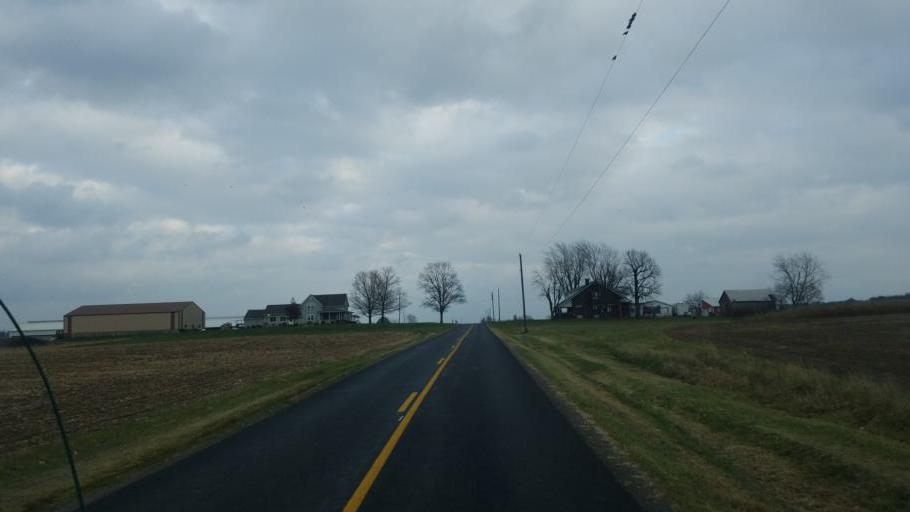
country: US
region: Ohio
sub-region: Mercer County
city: Fort Recovery
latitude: 40.5090
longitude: -84.7361
